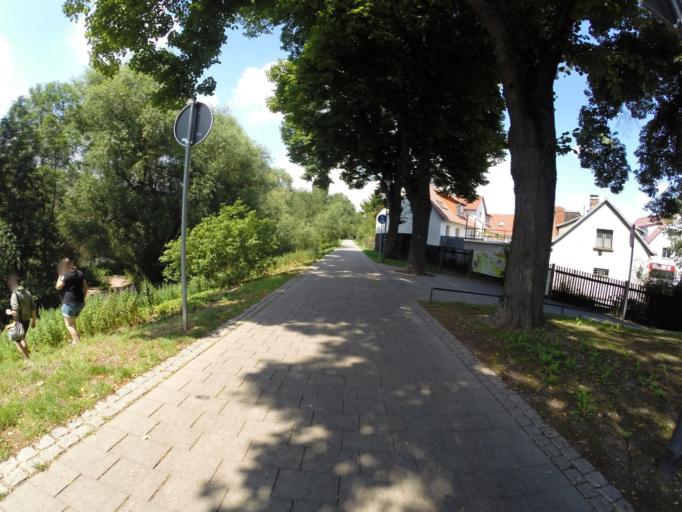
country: DE
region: Thuringia
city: Jena
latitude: 50.9308
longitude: 11.5968
